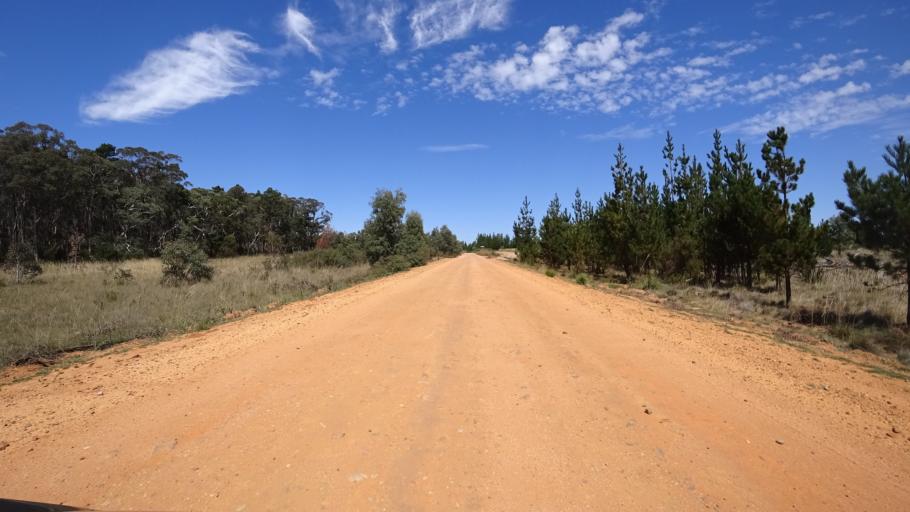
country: AU
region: New South Wales
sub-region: Lithgow
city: Lithgow
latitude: -33.3475
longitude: 150.2553
